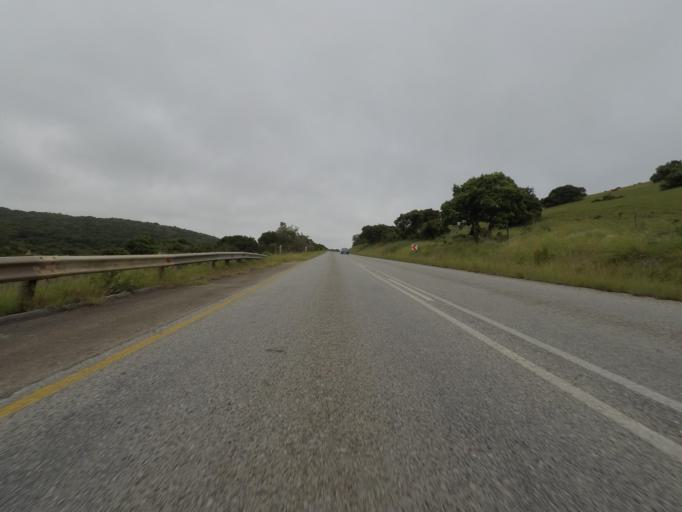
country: ZA
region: Eastern Cape
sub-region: Cacadu District Municipality
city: Port Alfred
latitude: -33.6128
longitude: 26.8052
